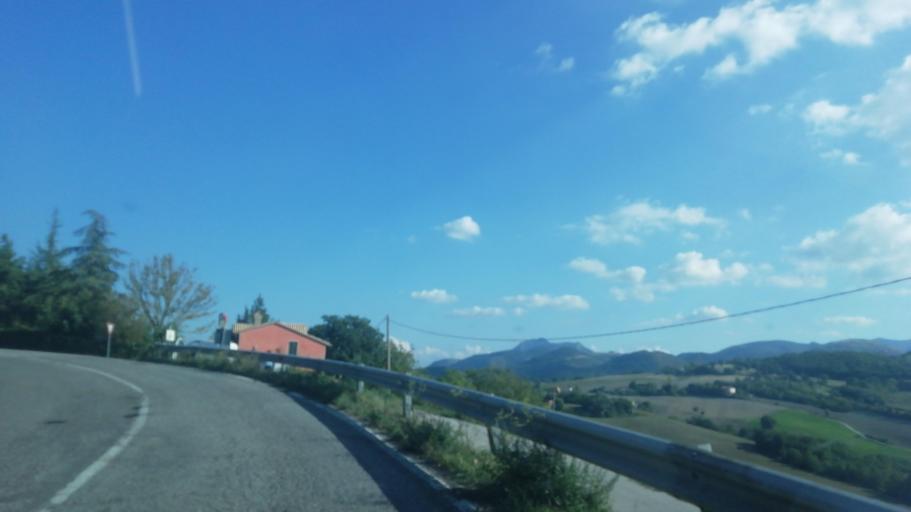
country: IT
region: The Marches
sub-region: Provincia di Pesaro e Urbino
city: Frontone
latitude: 43.5392
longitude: 12.7301
